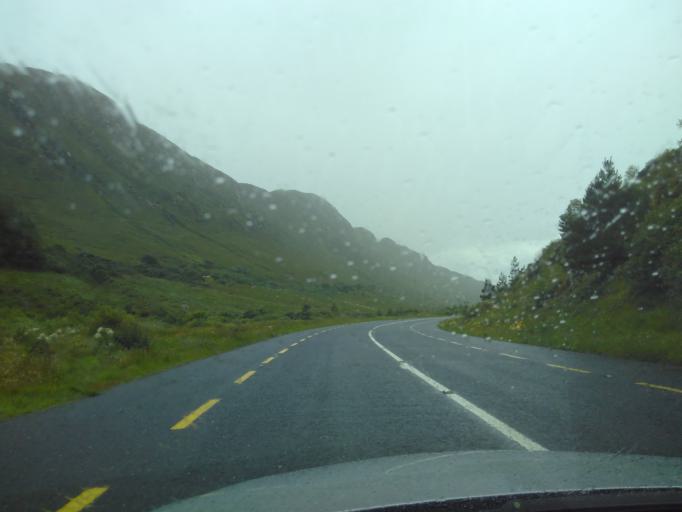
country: IE
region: Ulster
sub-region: County Donegal
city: Ballybofey
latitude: 54.7258
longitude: -7.9447
